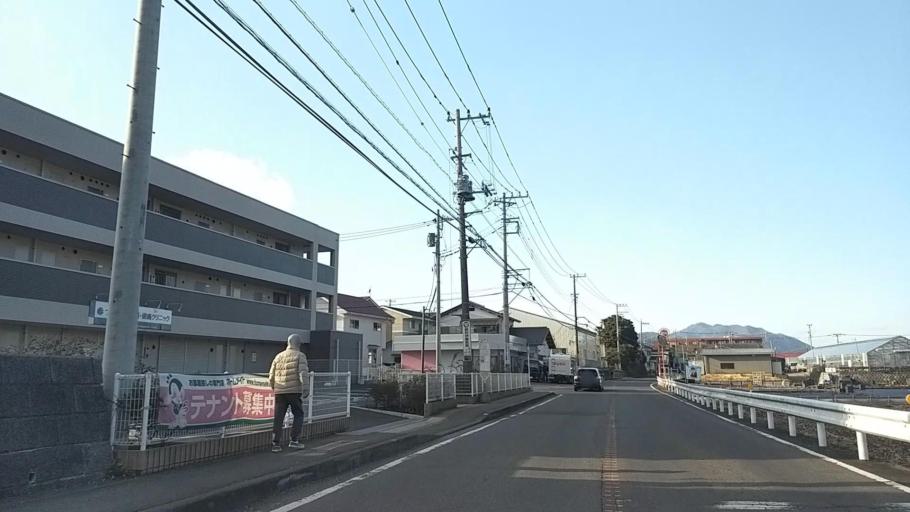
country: JP
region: Kanagawa
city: Atsugi
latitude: 35.4410
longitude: 139.3367
